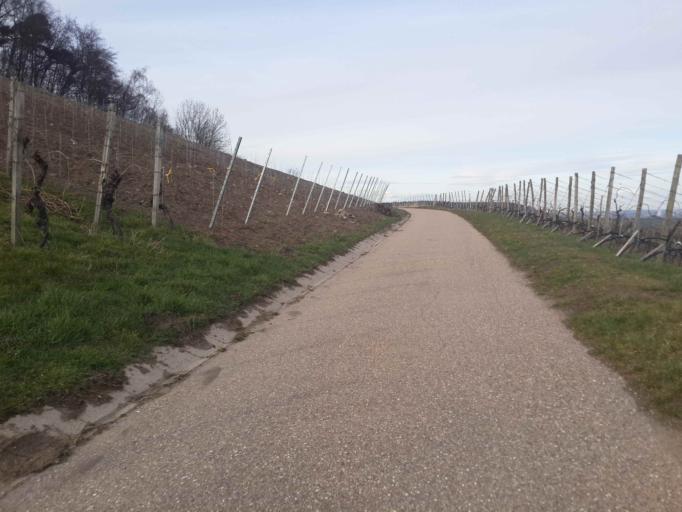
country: DE
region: Baden-Wuerttemberg
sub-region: Regierungsbezirk Stuttgart
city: Brackenheim
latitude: 49.1019
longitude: 9.0772
